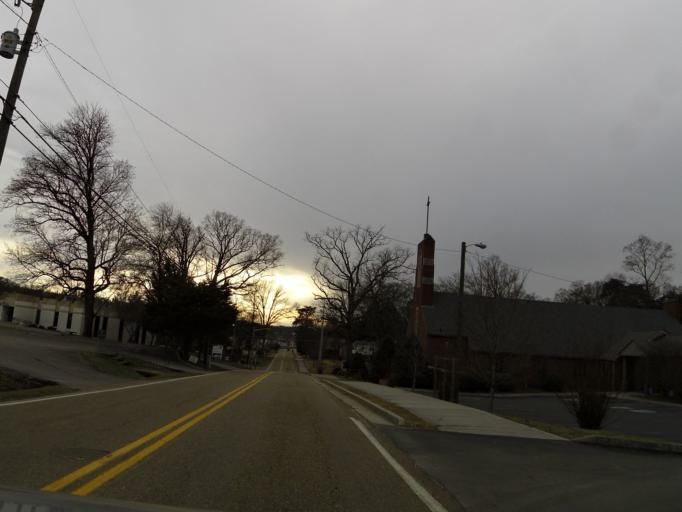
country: US
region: Tennessee
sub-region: Knox County
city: Knoxville
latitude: 35.9381
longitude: -83.9923
